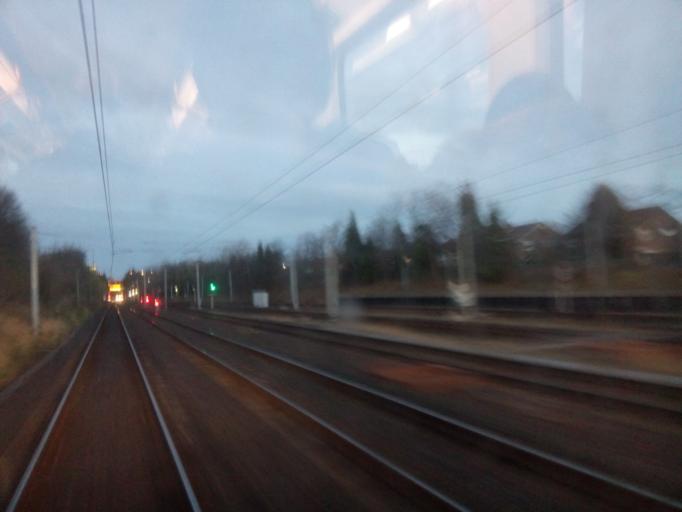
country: GB
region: England
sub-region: Newcastle upon Tyne
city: Gosforth
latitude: 55.0109
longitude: -1.6150
